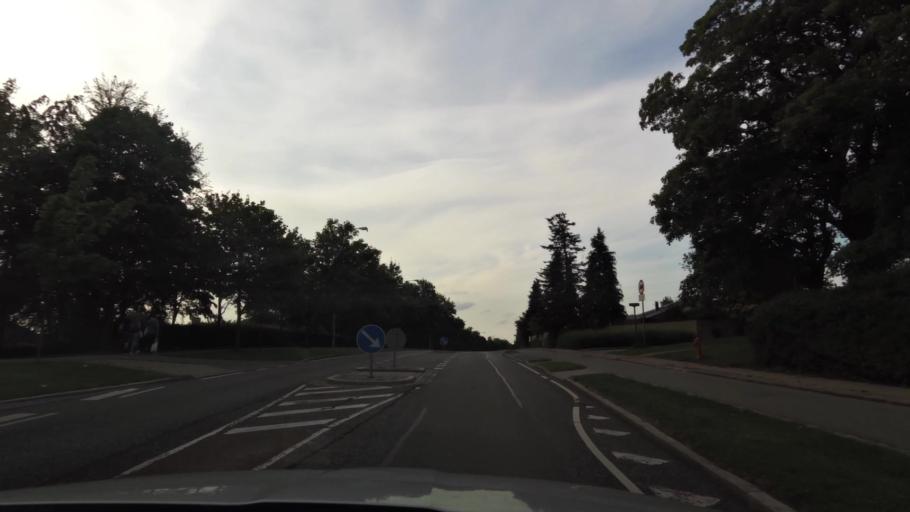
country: DK
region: Capital Region
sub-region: Rudersdal Kommune
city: Birkerod
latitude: 55.8343
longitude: 12.4185
